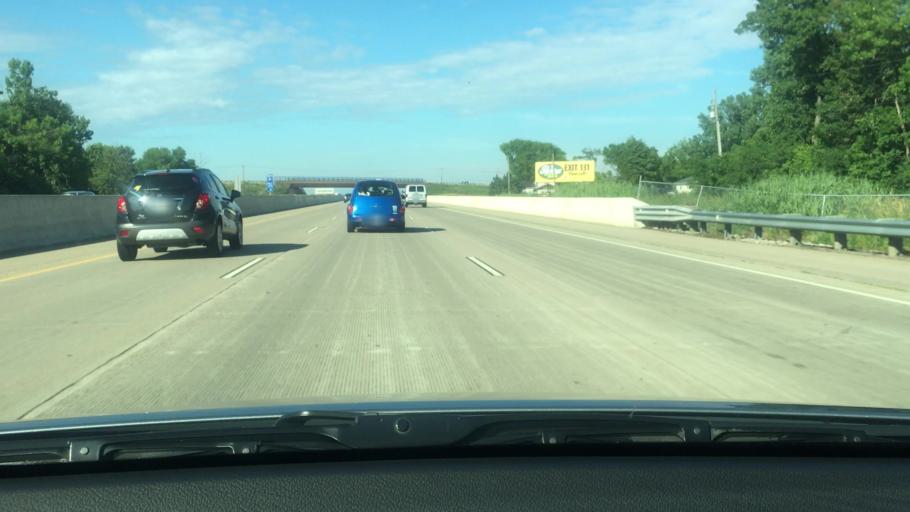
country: US
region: Wisconsin
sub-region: Winnebago County
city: Oshkosh
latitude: 44.1101
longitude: -88.5239
